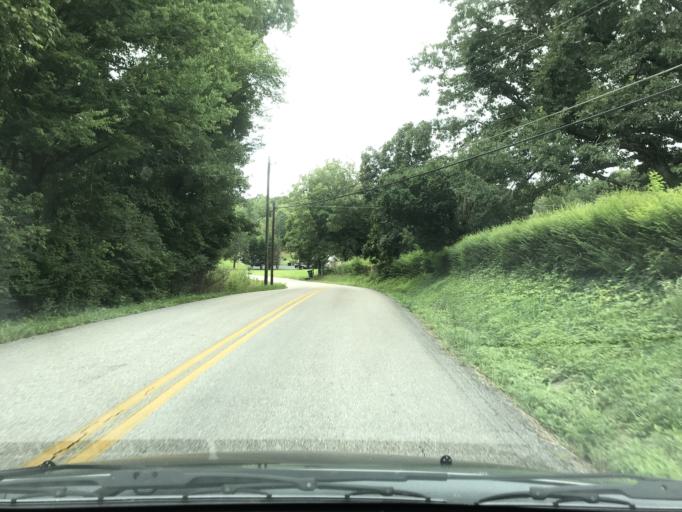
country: US
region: Tennessee
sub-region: Hamilton County
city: Lakesite
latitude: 35.1722
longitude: -85.0799
